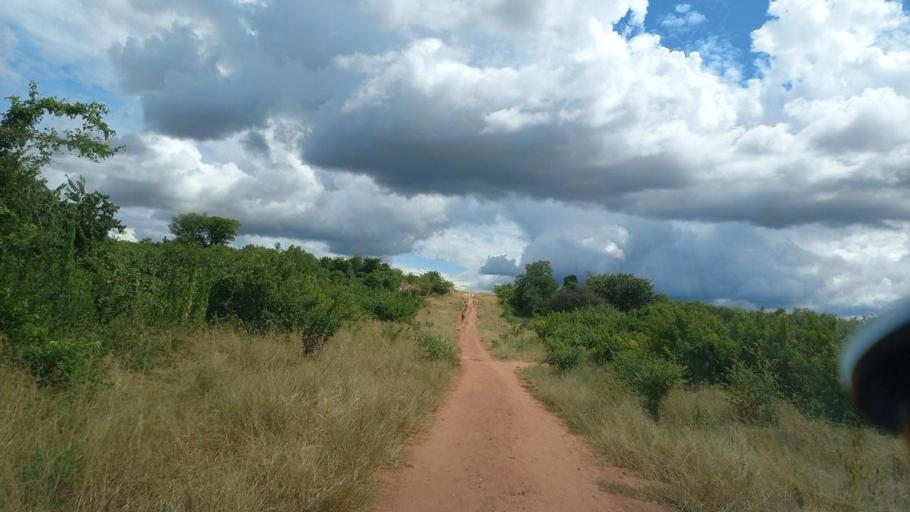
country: ZM
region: Lusaka
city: Luangwa
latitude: -15.6243
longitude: 30.3940
